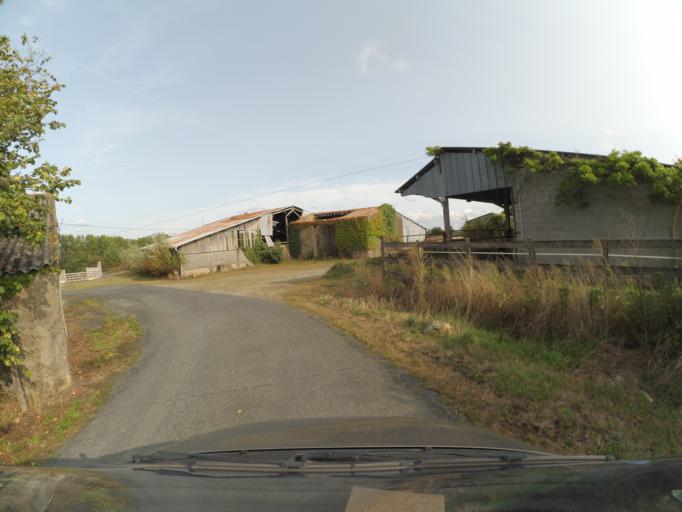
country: FR
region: Pays de la Loire
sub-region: Departement de la Vendee
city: Saint-Hilaire-de-Loulay
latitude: 47.0074
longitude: -1.3588
